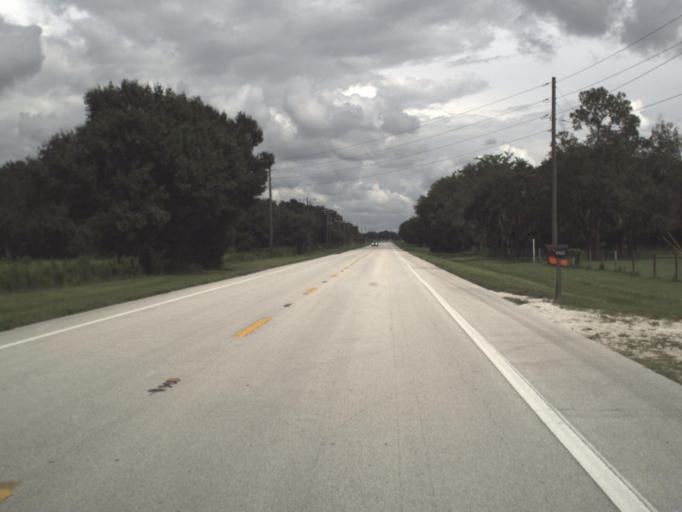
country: US
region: Florida
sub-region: DeSoto County
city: Nocatee
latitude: 27.2007
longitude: -81.9756
